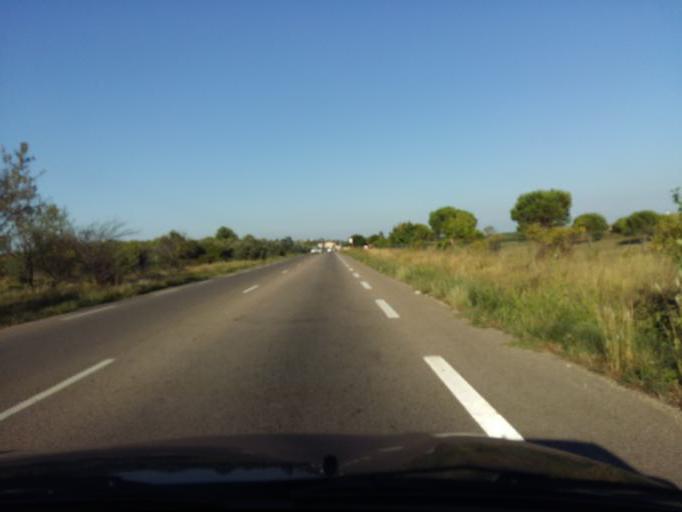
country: FR
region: Languedoc-Roussillon
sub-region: Departement du Gard
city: Saint-Gervasy
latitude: 43.8714
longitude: 4.4588
